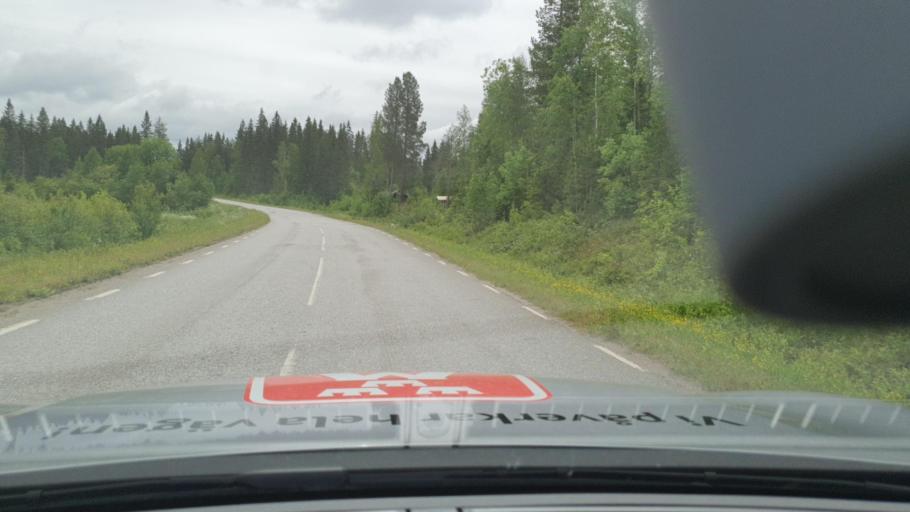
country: SE
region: Norrbotten
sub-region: Lulea Kommun
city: Ranea
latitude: 65.8759
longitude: 22.2153
